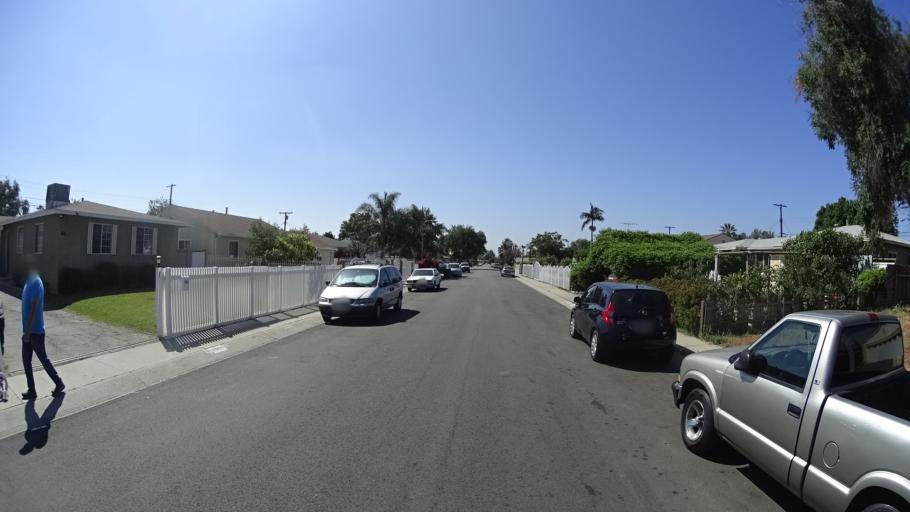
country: US
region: California
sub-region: Los Angeles County
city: Van Nuys
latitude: 34.2271
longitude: -118.4468
